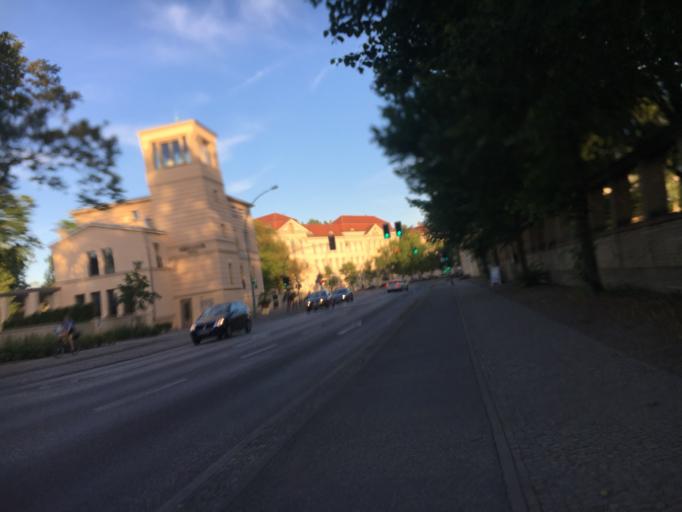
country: DE
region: Brandenburg
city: Potsdam
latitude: 52.4021
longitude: 13.0458
